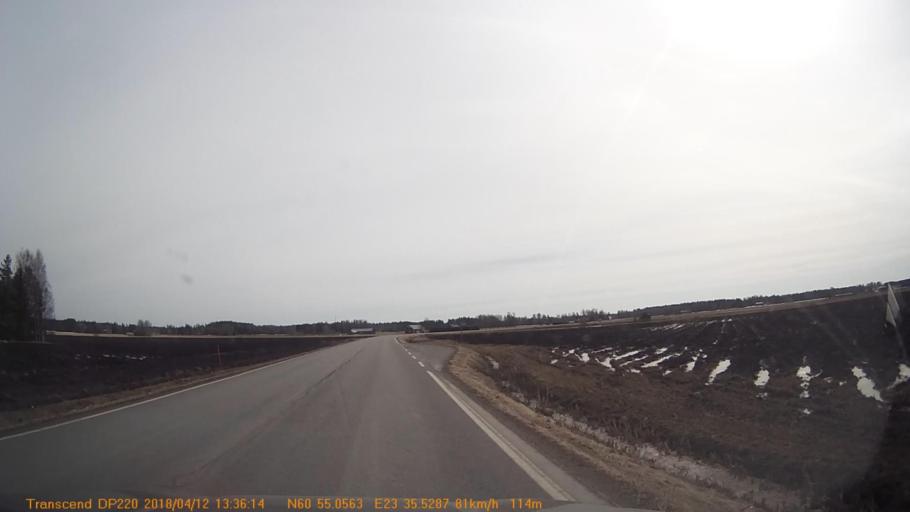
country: FI
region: Haeme
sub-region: Forssa
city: Forssa
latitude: 60.9173
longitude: 23.5924
